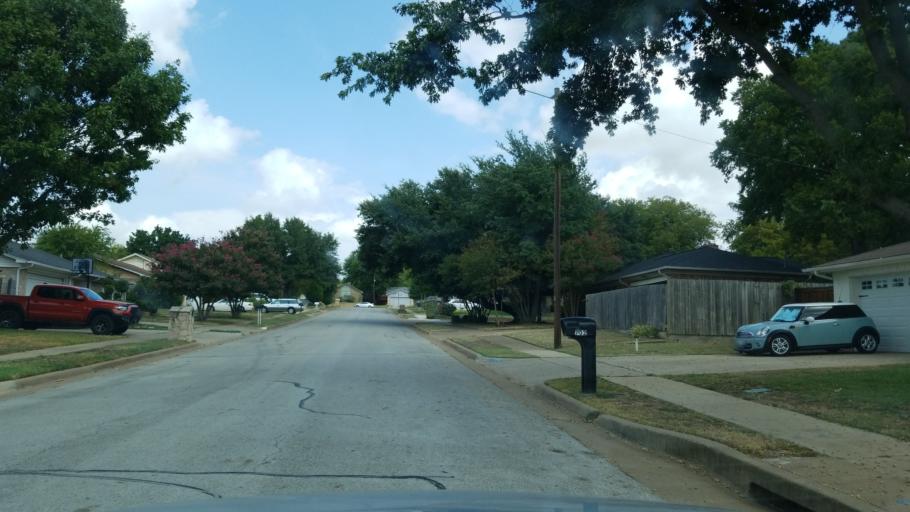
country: US
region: Texas
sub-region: Tarrant County
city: Euless
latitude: 32.8463
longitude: -97.0982
